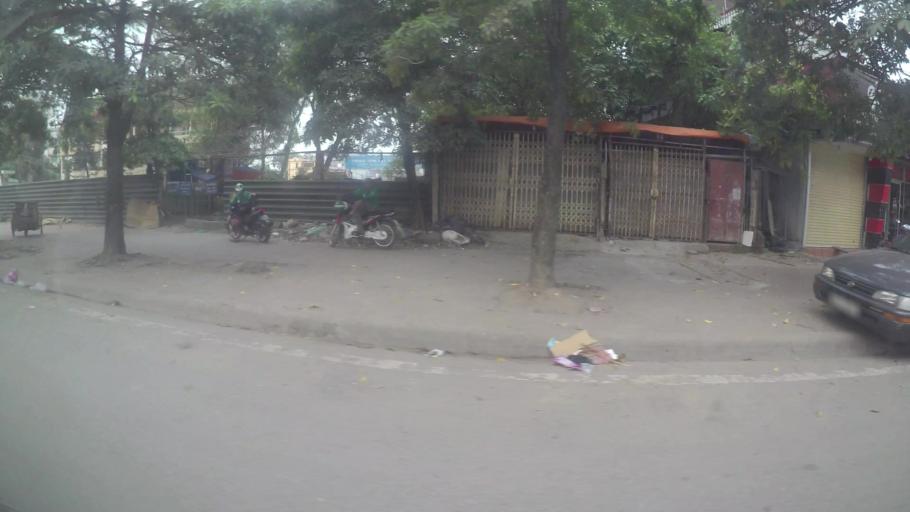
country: VN
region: Ha Noi
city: Cau Dien
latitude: 21.0514
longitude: 105.7372
